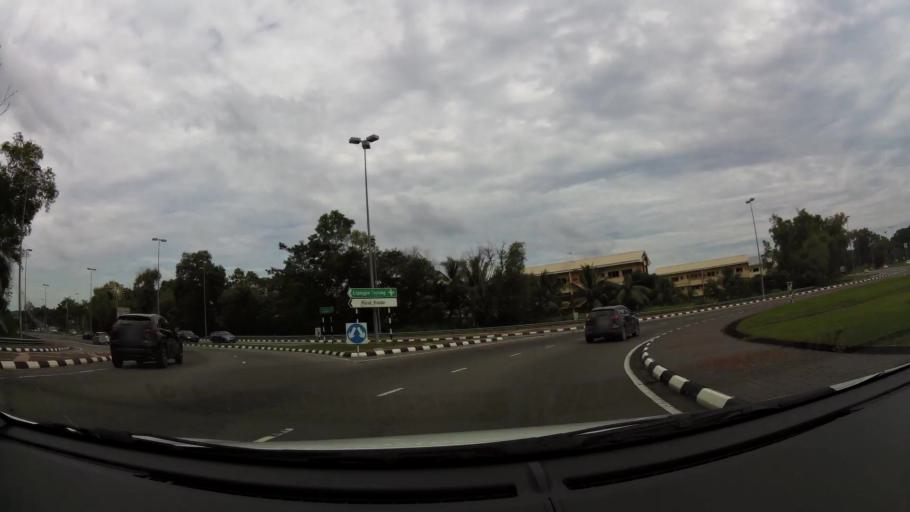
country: BN
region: Brunei and Muara
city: Bandar Seri Begawan
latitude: 4.8963
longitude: 114.9114
